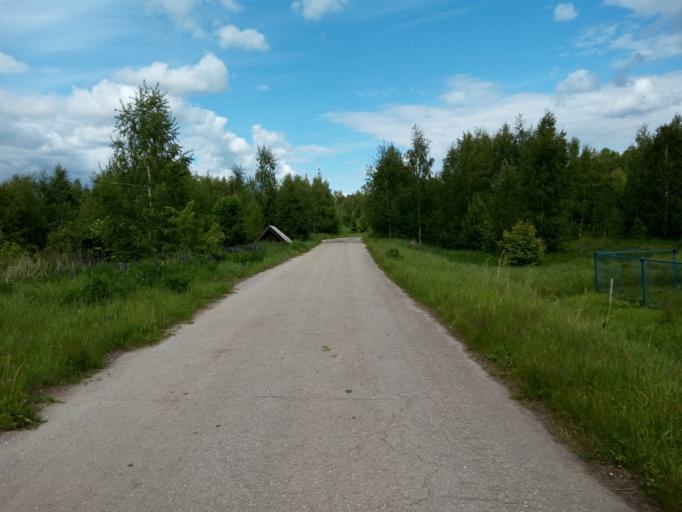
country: RU
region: Nizjnij Novgorod
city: Voskresenskoye
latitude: 56.7714
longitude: 45.5560
